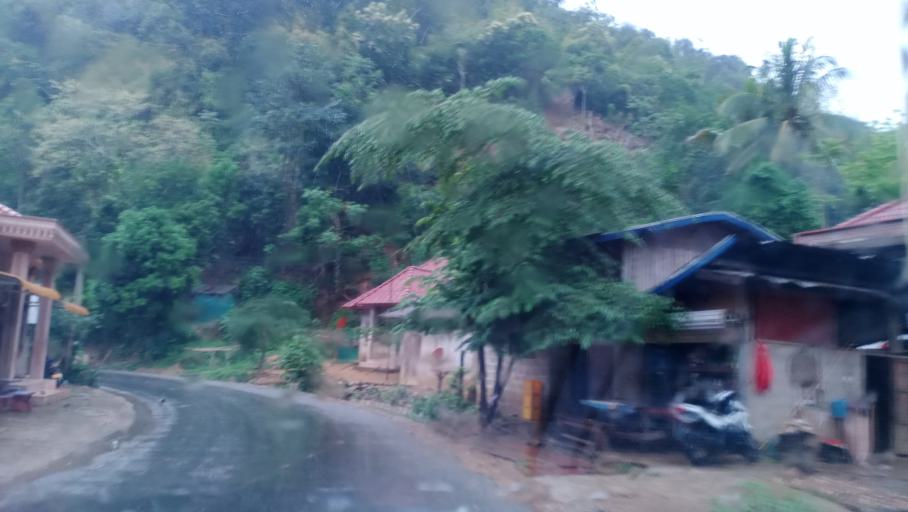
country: LA
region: Phongsali
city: Khoa
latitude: 21.0601
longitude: 102.4650
